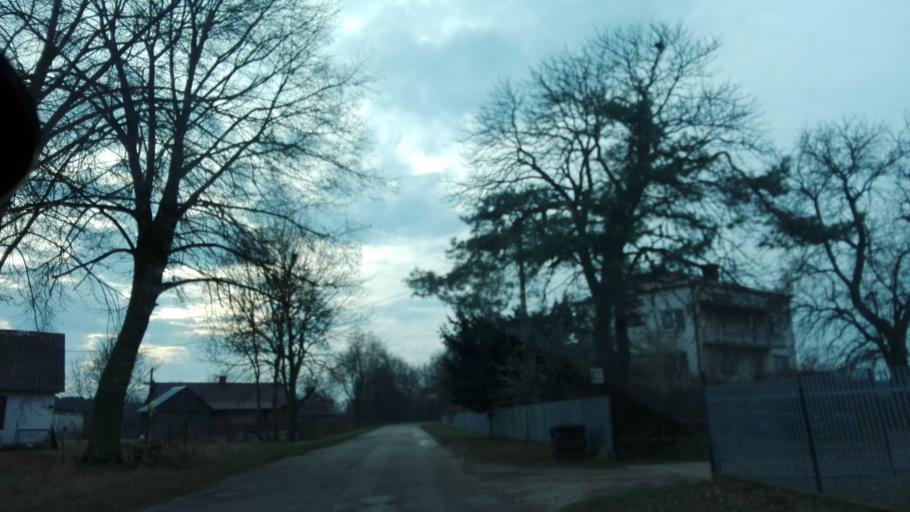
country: PL
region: Lublin Voivodeship
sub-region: Powiat bialski
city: Sosnowka
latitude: 51.7237
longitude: 23.4354
